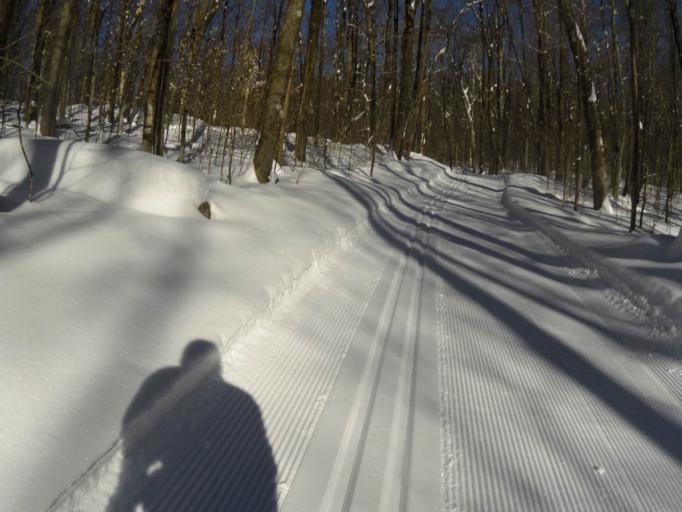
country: CA
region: Quebec
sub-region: Outaouais
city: Wakefield
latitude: 45.5859
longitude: -75.9656
